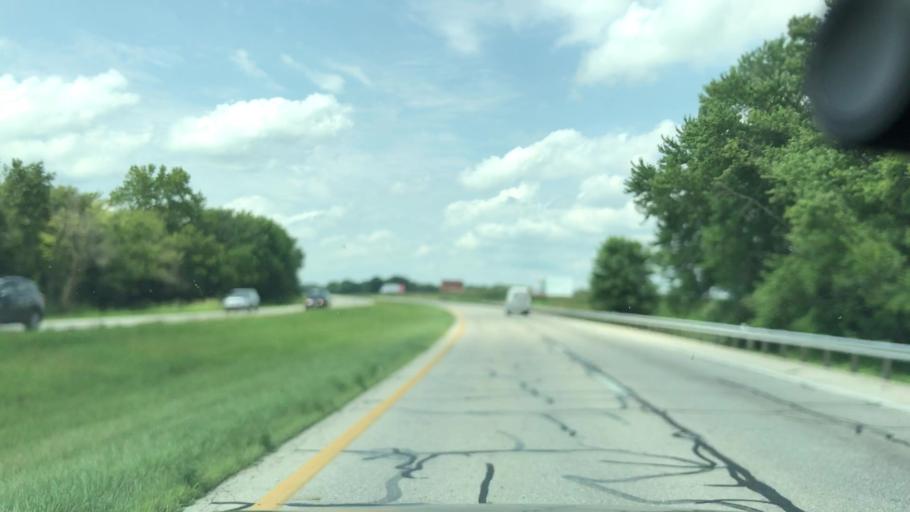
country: US
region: Ohio
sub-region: Ross County
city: Kingston
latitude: 39.4894
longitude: -82.9716
